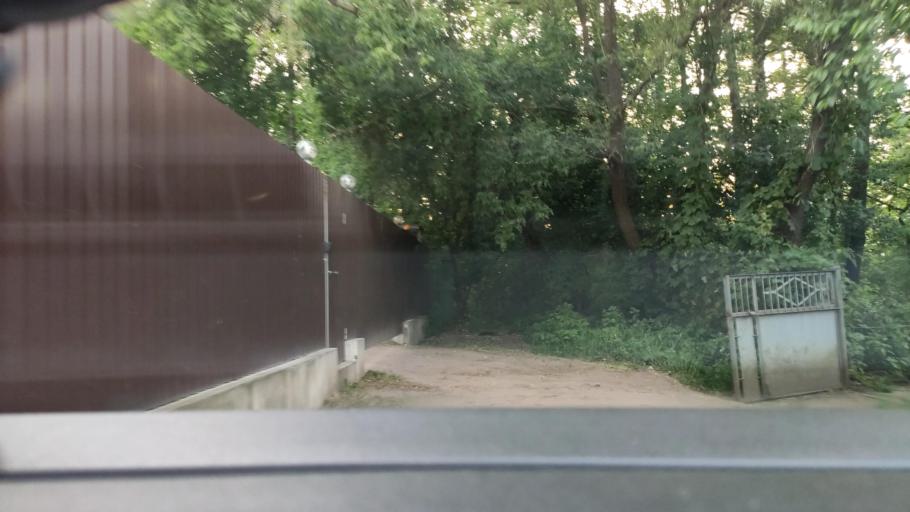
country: RU
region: Voronezj
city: Pridonskoy
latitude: 51.6429
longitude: 39.0815
